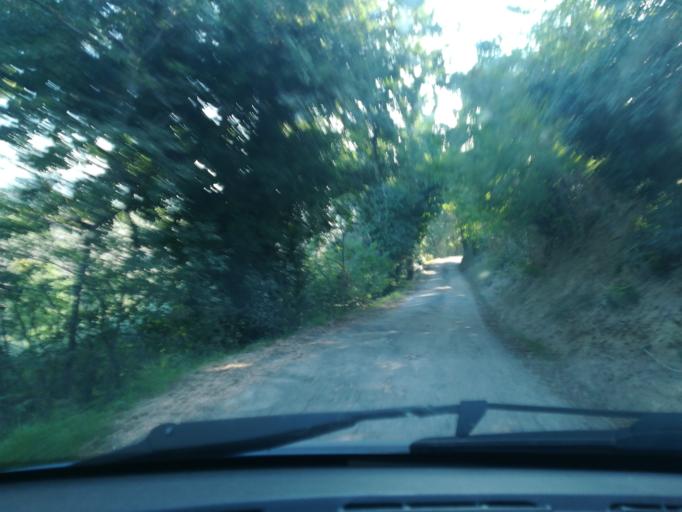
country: IT
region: The Marches
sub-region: Provincia di Macerata
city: Macerata
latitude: 43.2853
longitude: 13.4576
